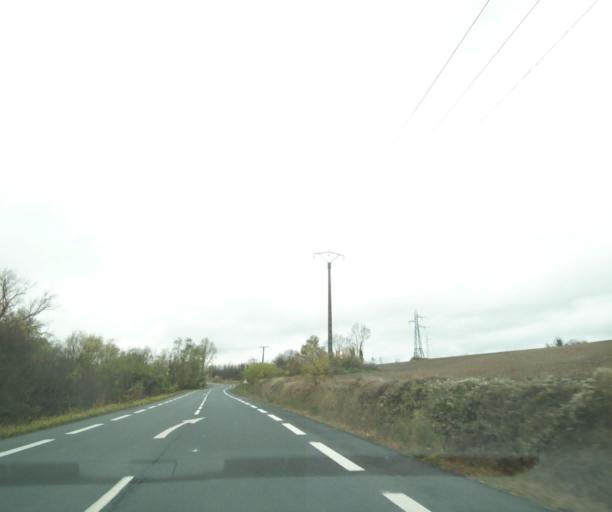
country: FR
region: Auvergne
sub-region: Departement du Puy-de-Dome
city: Dallet
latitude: 45.7772
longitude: 3.2355
